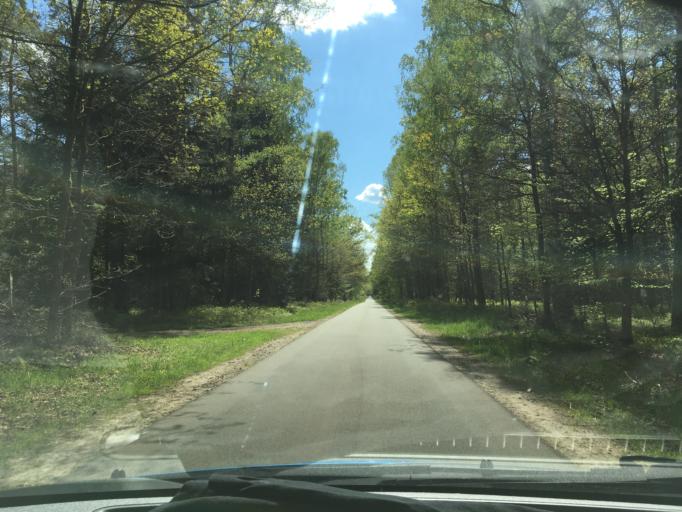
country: DE
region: Lower Saxony
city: Boitze
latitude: 53.1250
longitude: 10.7947
